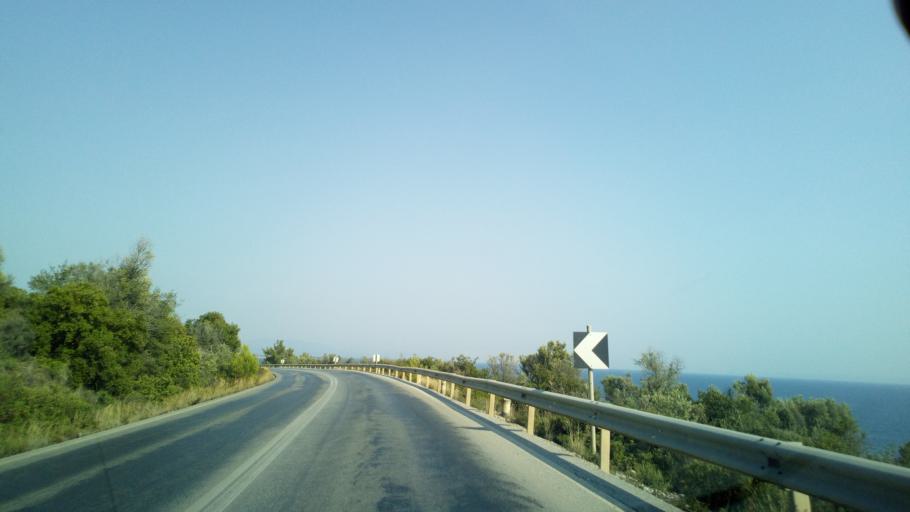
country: GR
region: Central Macedonia
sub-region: Nomos Chalkidikis
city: Ormylia
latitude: 40.2611
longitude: 23.4741
